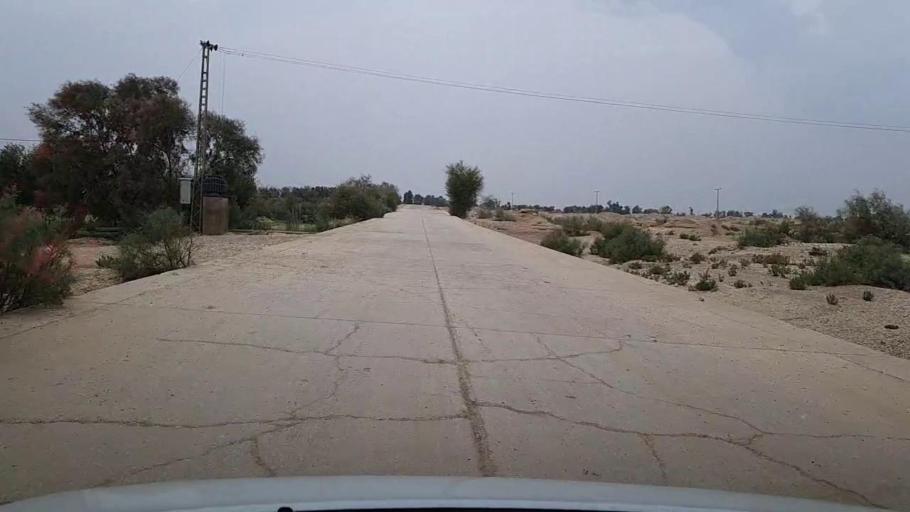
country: PK
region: Sindh
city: Sehwan
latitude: 26.3174
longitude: 67.7444
